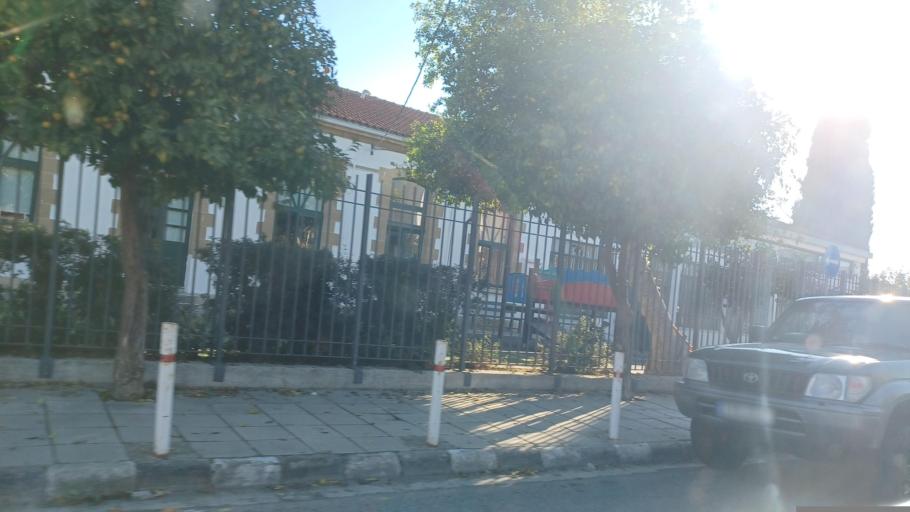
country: CY
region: Lefkosia
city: Nicosia
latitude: 35.1500
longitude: 33.3397
